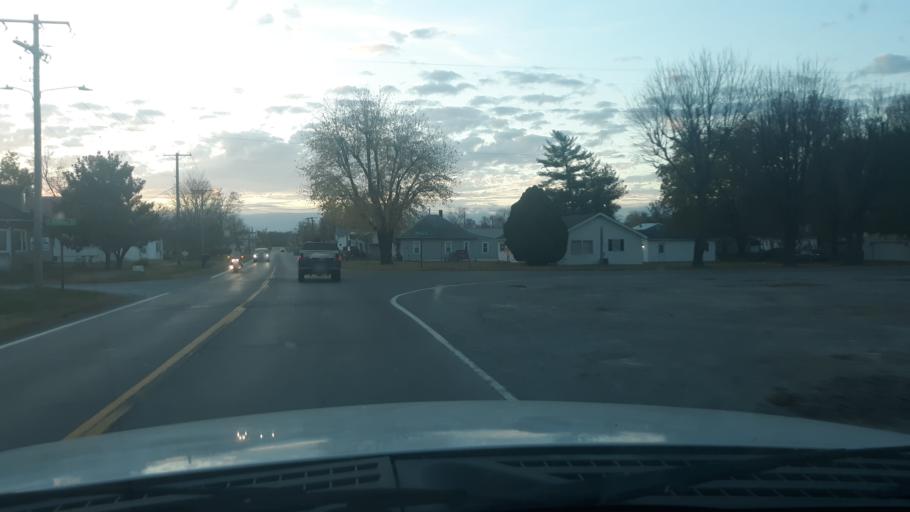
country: US
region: Illinois
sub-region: Saline County
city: Harrisburg
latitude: 37.8406
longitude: -88.6050
